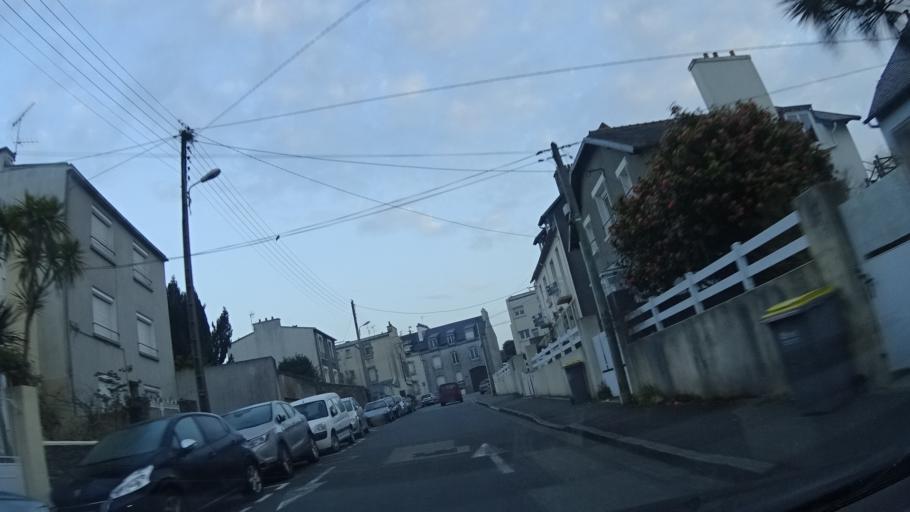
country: FR
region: Brittany
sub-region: Departement du Finistere
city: Brest
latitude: 48.3982
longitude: -4.4592
